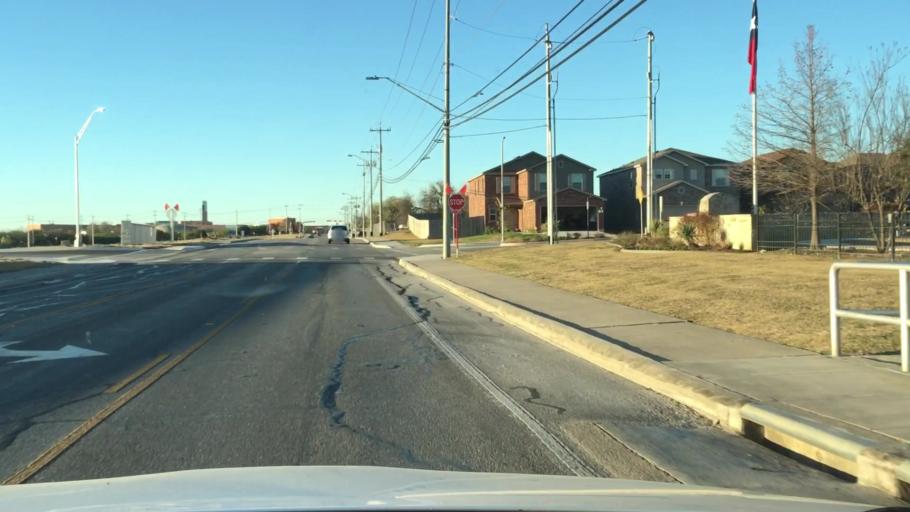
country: US
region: Texas
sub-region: Bexar County
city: Converse
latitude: 29.5405
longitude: -98.3180
